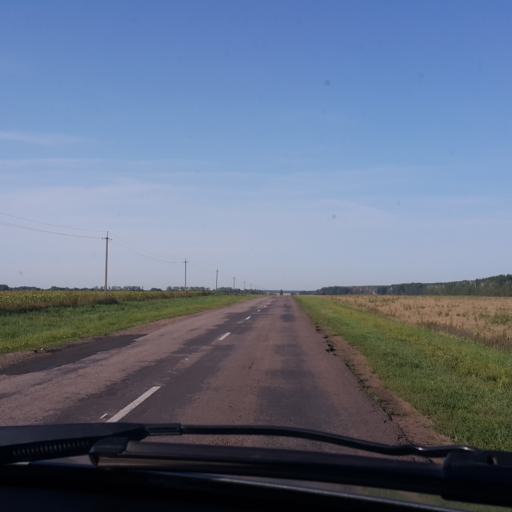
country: RU
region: Tambov
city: Novaya Lyada
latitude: 52.7677
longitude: 41.7410
